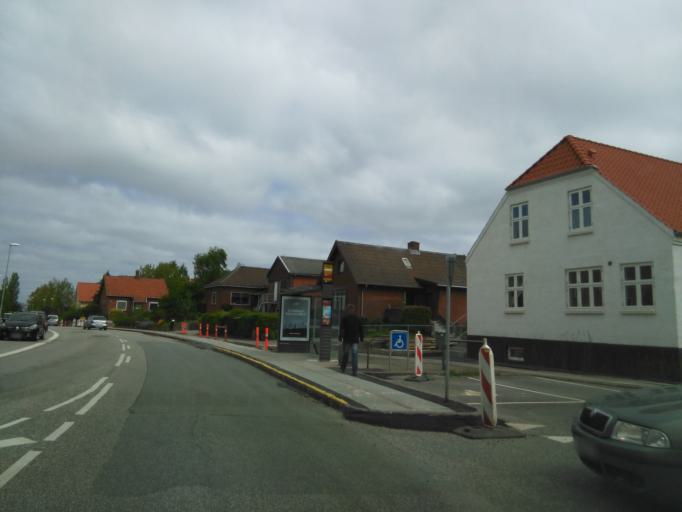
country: DK
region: Central Jutland
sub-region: Arhus Kommune
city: Marslet
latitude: 56.1156
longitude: 10.1742
